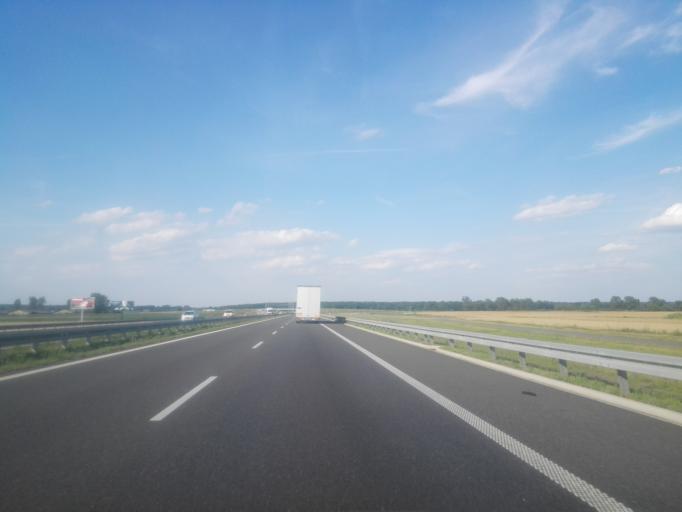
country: PL
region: Lower Silesian Voivodeship
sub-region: Powiat olesnicki
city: Twardogora
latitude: 51.2792
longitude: 17.5656
